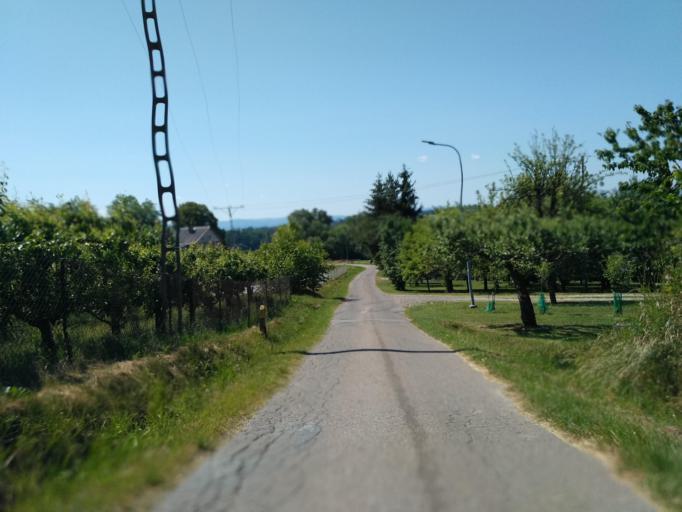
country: PL
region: Subcarpathian Voivodeship
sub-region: Powiat krosnienski
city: Korczyna
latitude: 49.7282
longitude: 21.7815
